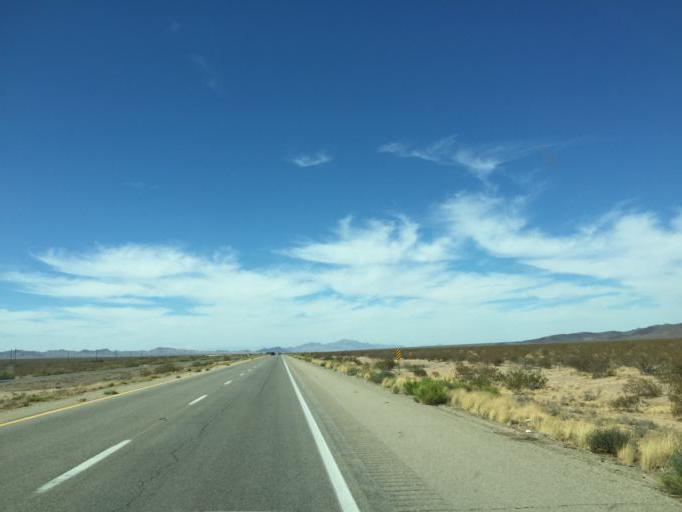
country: US
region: Arizona
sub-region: Mohave County
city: Dolan Springs
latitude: 35.5960
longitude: -114.3982
